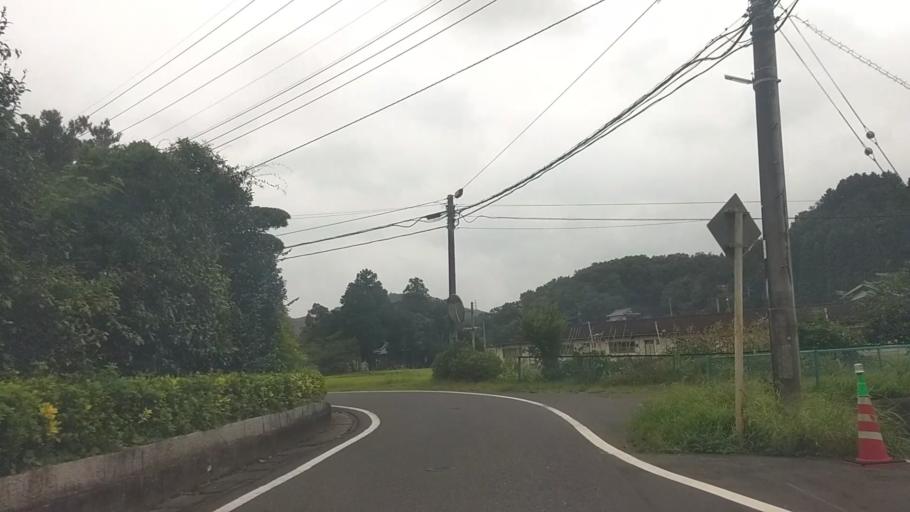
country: JP
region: Chiba
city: Kawaguchi
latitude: 35.2545
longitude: 140.0587
